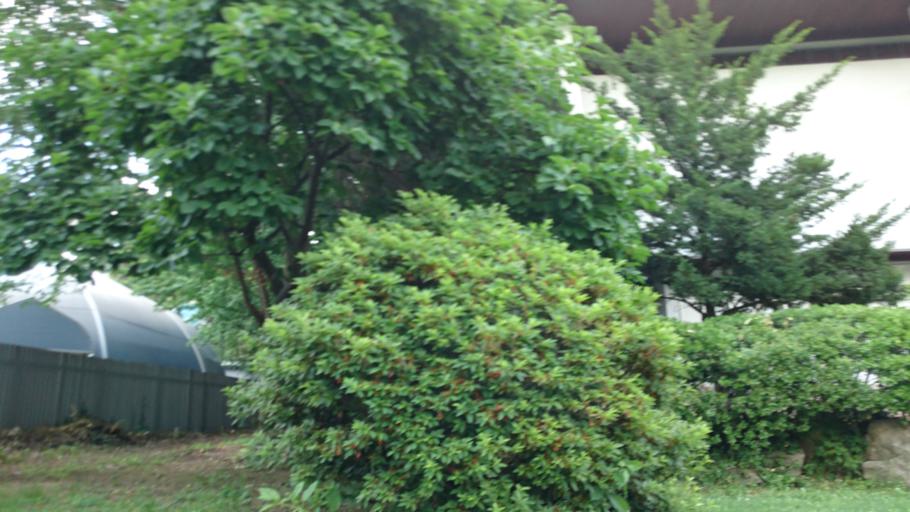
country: KR
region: Seoul
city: Seoul
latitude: 37.5421
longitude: 126.9801
